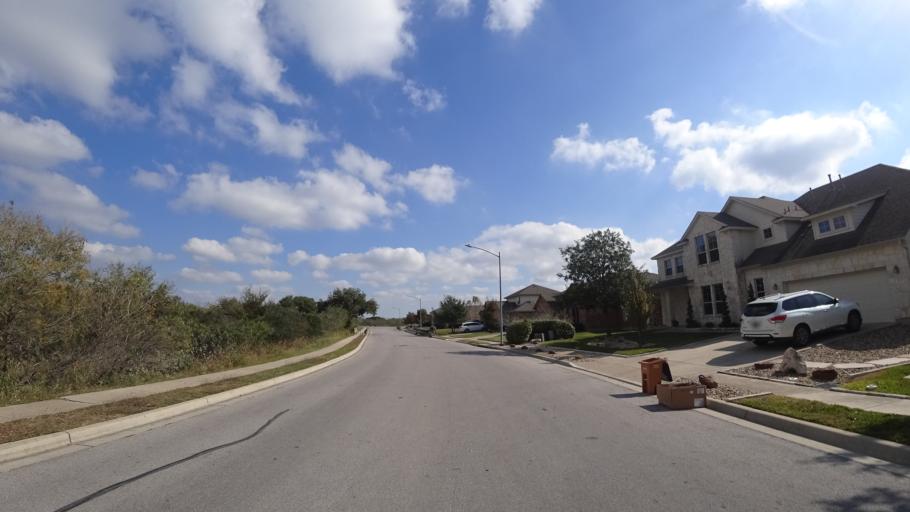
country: US
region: Texas
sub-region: Travis County
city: Shady Hollow
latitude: 30.1599
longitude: -97.8466
